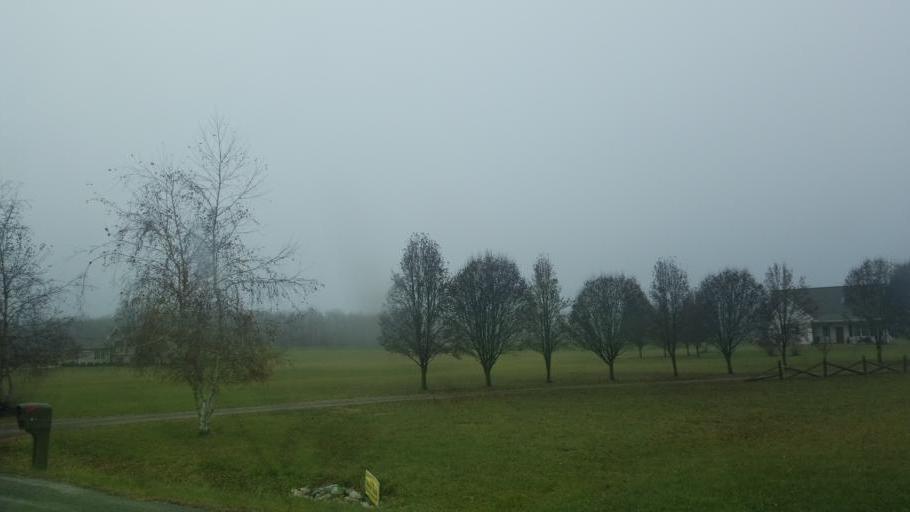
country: US
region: Ohio
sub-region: Champaign County
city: North Lewisburg
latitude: 40.2752
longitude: -83.6022
